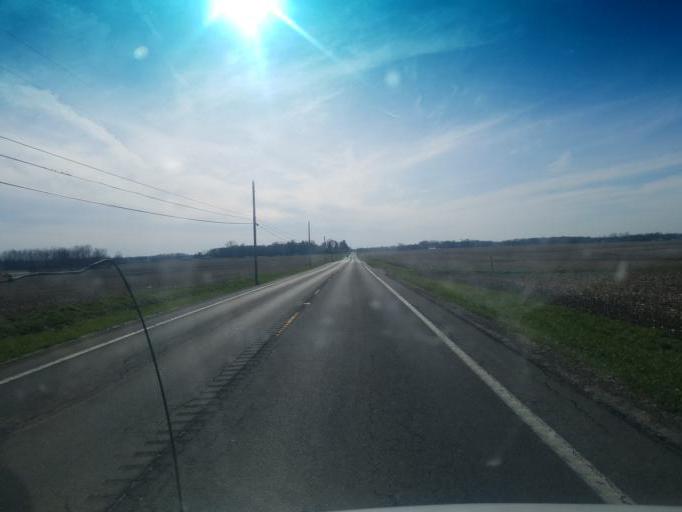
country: US
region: Ohio
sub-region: Logan County
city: Bellefontaine
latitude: 40.3653
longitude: -83.8259
